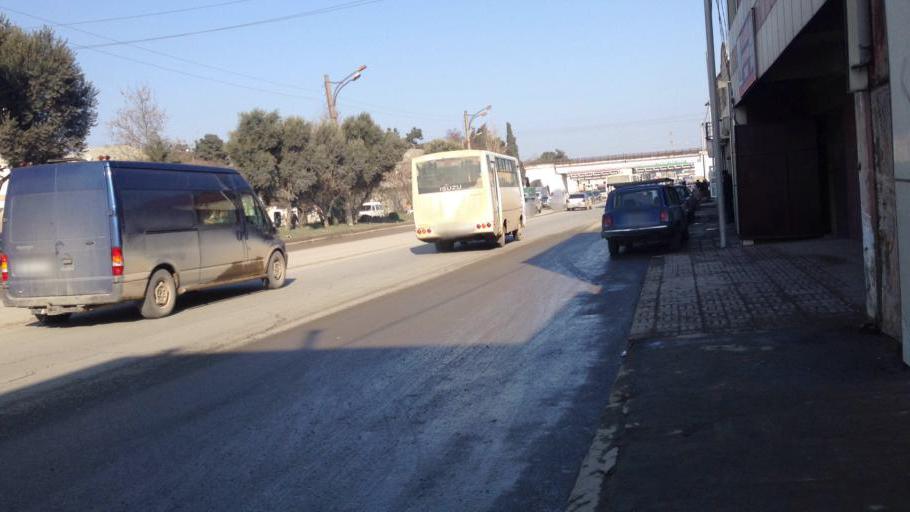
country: AZ
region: Baki
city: Binagadi
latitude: 40.4380
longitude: 49.8447
